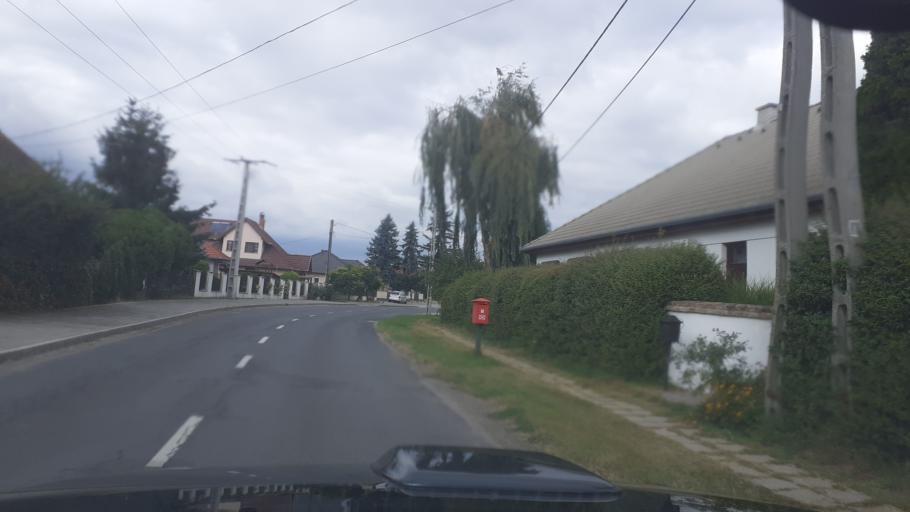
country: HU
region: Fejer
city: Racalmas
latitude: 47.0269
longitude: 18.9383
